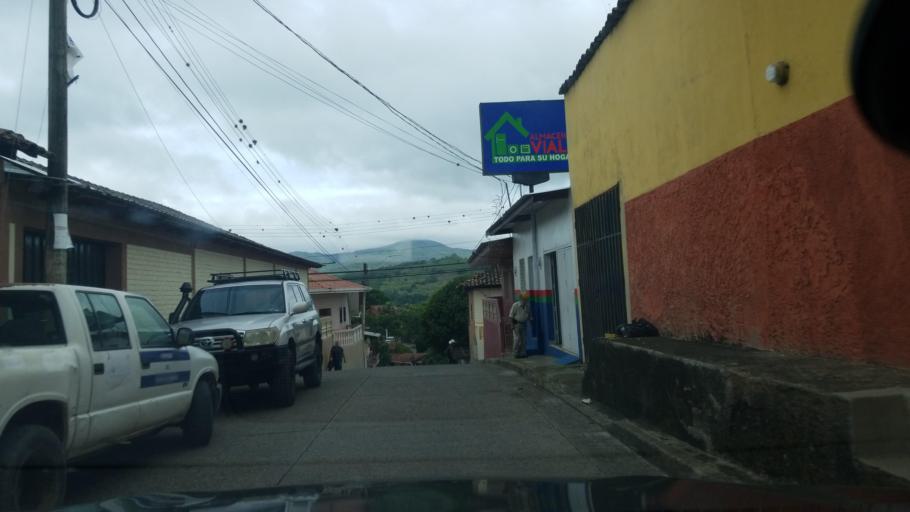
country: HN
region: Choluteca
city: San Marcos de Colon
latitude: 13.4323
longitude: -86.8102
